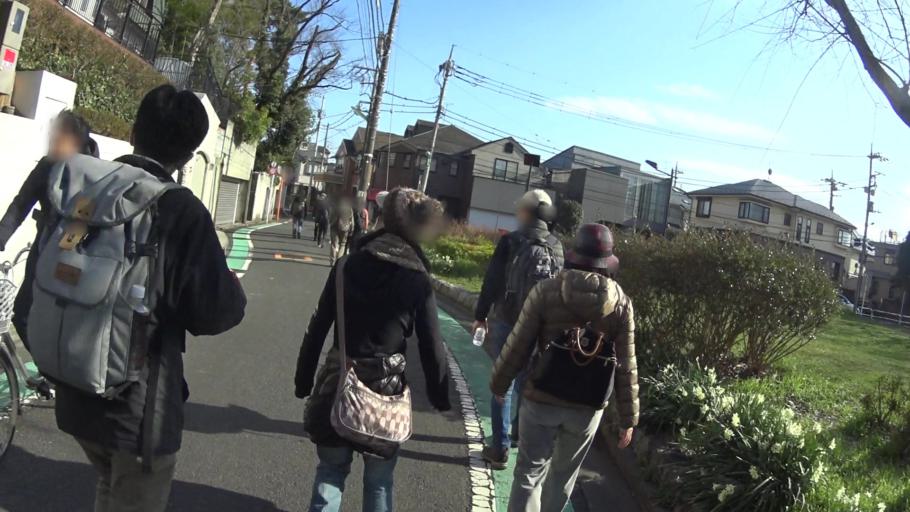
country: JP
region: Tokyo
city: Mitaka-shi
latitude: 35.6532
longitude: 139.6012
